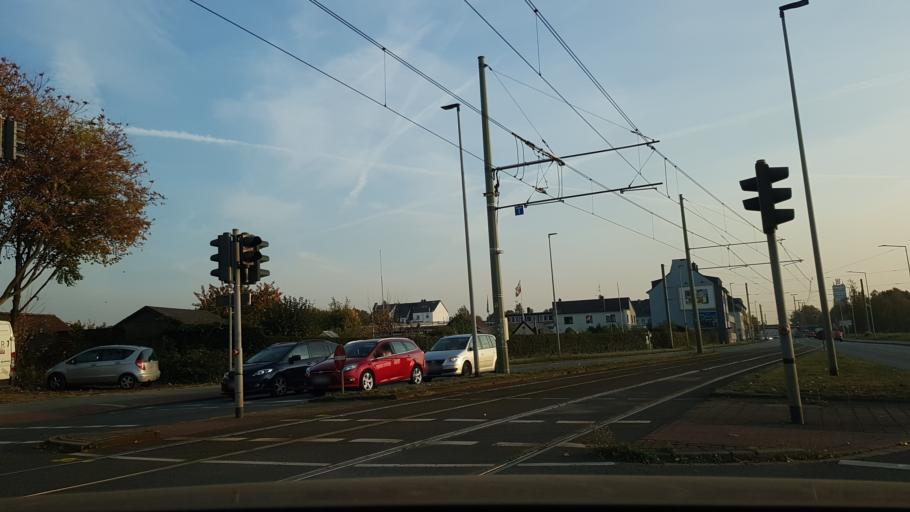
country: DE
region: North Rhine-Westphalia
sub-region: Regierungsbezirk Dusseldorf
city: Hochfeld
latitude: 51.4126
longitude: 6.7527
